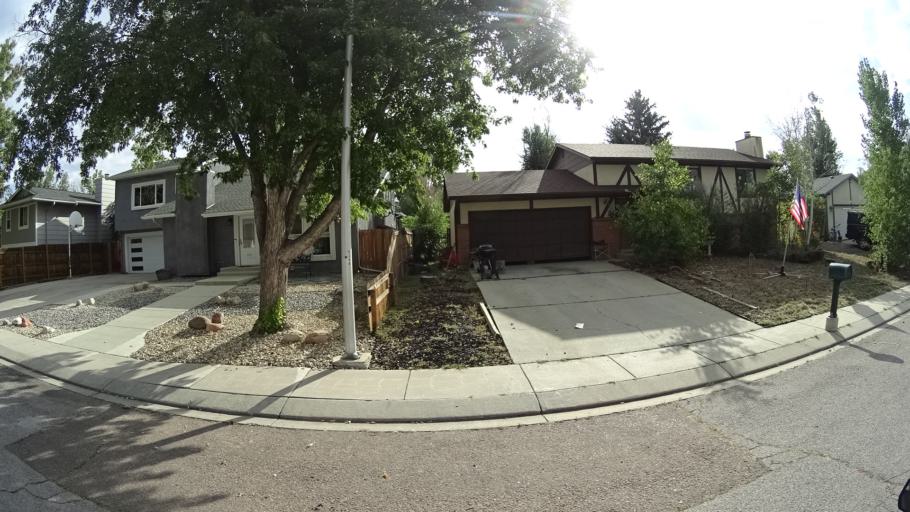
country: US
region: Colorado
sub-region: El Paso County
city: Cimarron Hills
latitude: 38.8583
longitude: -104.7524
